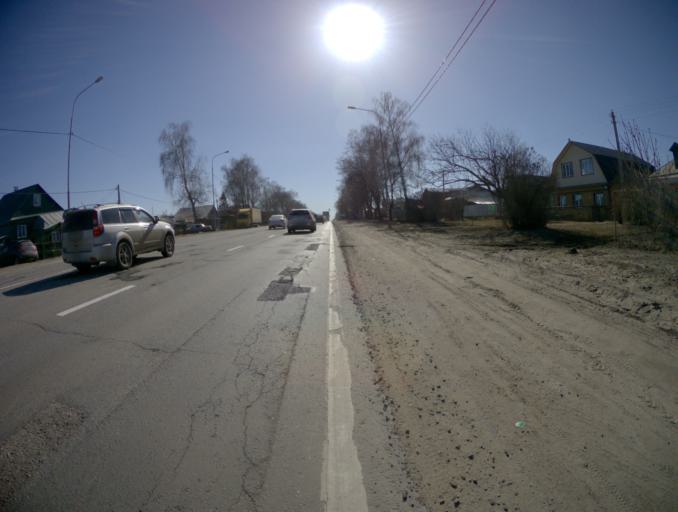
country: RU
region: Vladimir
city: Bogolyubovo
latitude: 56.1887
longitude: 40.5214
